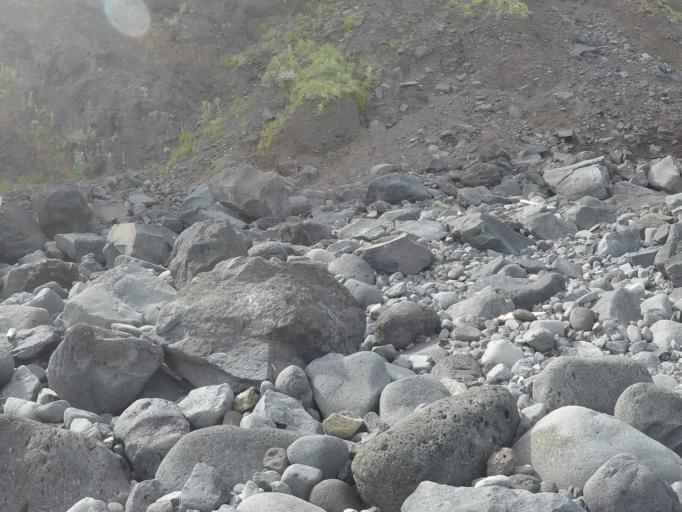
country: PT
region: Madeira
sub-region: Sao Vicente
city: Sao Vicente
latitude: 32.8274
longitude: -16.9969
